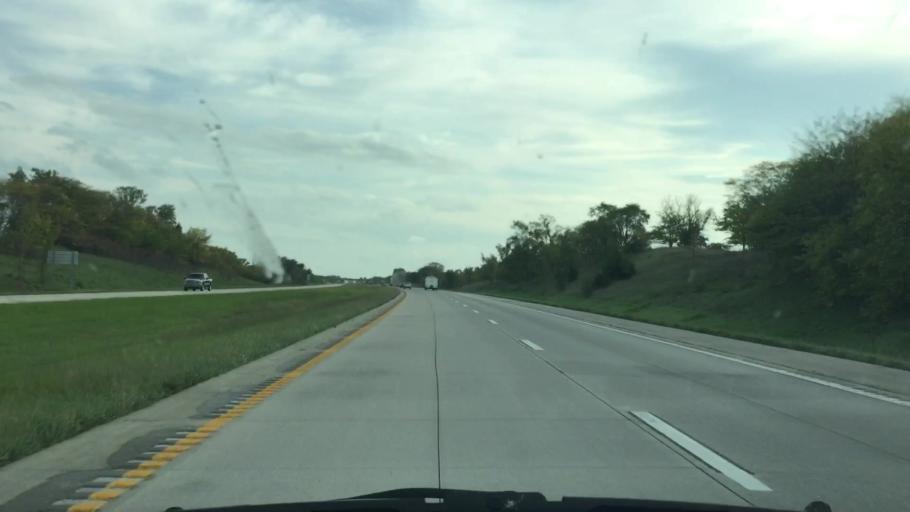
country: US
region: Missouri
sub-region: Daviess County
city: Gallatin
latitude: 40.0087
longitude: -94.0967
